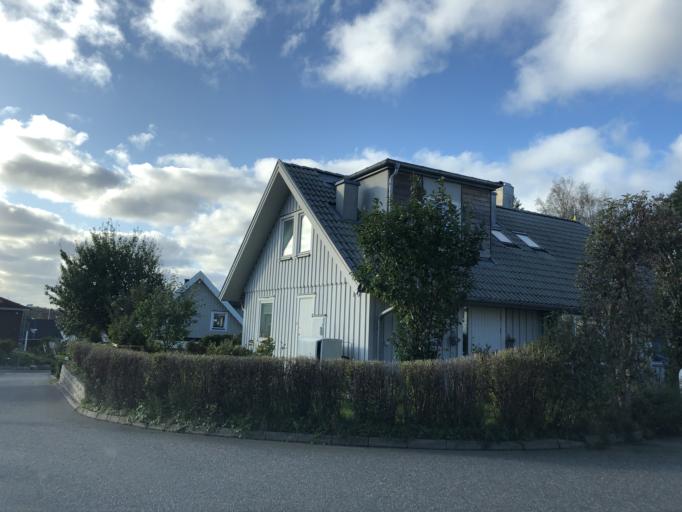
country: SE
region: Vaestra Goetaland
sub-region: Goteborg
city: Majorna
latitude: 57.6407
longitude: 11.8731
